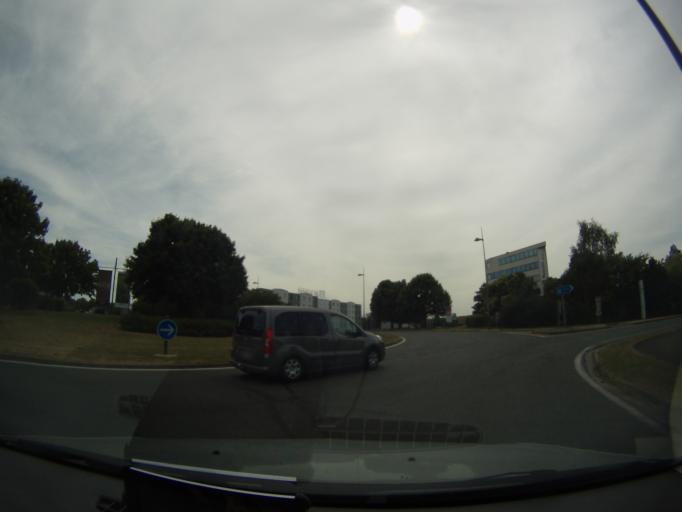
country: FR
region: Poitou-Charentes
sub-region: Departement de la Vienne
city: Jaunay-Clan
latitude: 46.6690
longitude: 0.3605
